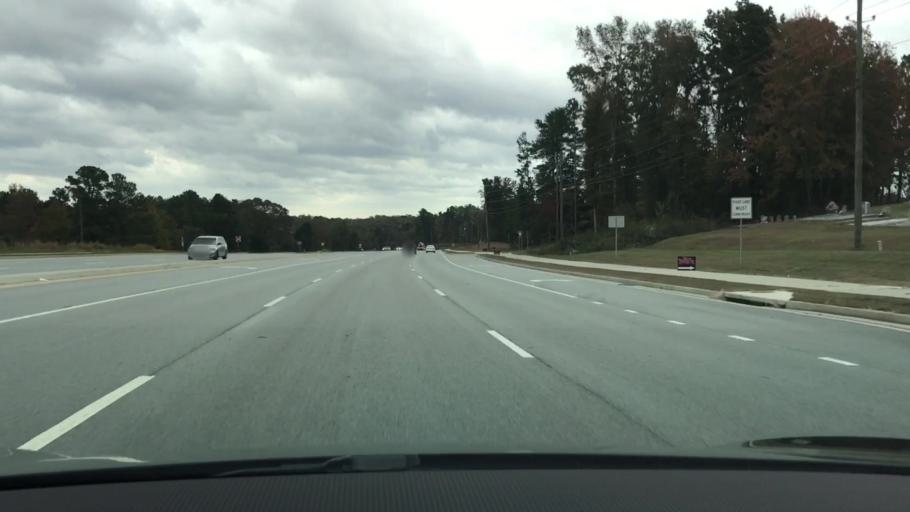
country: US
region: Georgia
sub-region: Hall County
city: Flowery Branch
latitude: 34.1278
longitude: -83.9229
